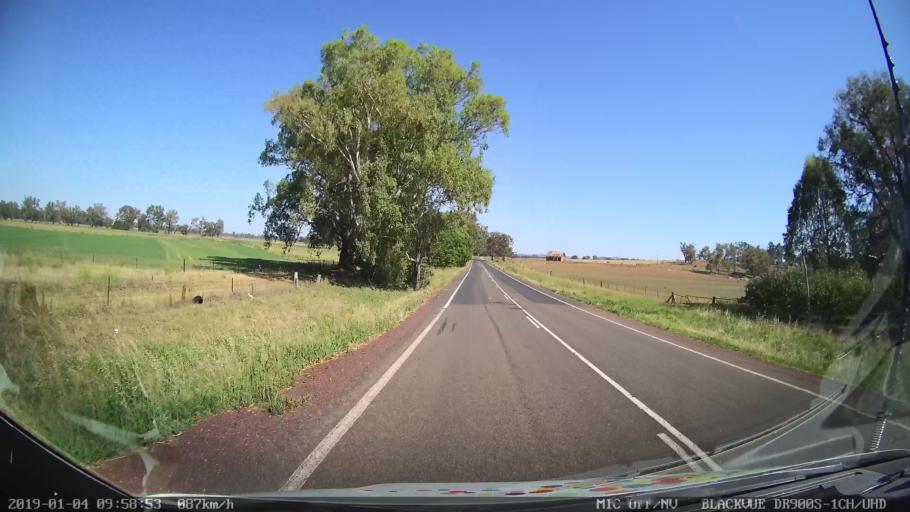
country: AU
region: New South Wales
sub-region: Cabonne
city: Canowindra
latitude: -33.5138
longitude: 148.3907
